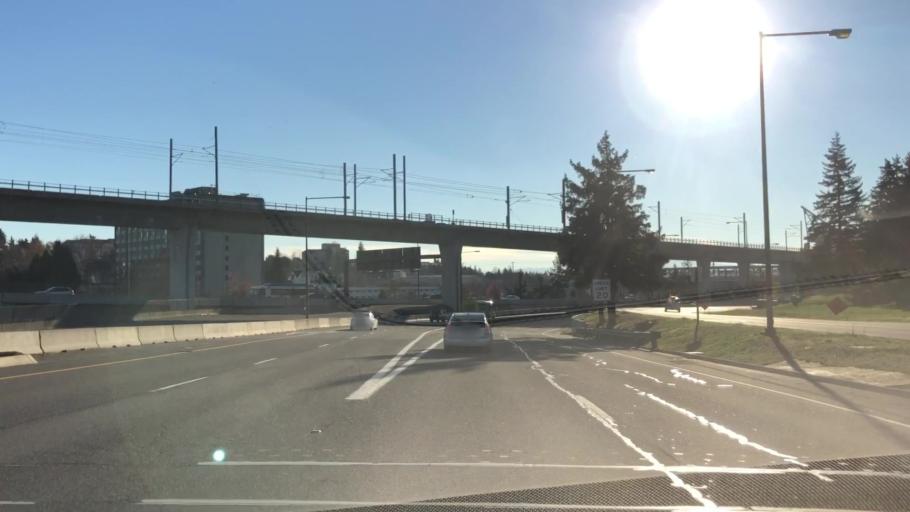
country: US
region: Washington
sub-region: King County
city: SeaTac
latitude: 47.4481
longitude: -122.2983
